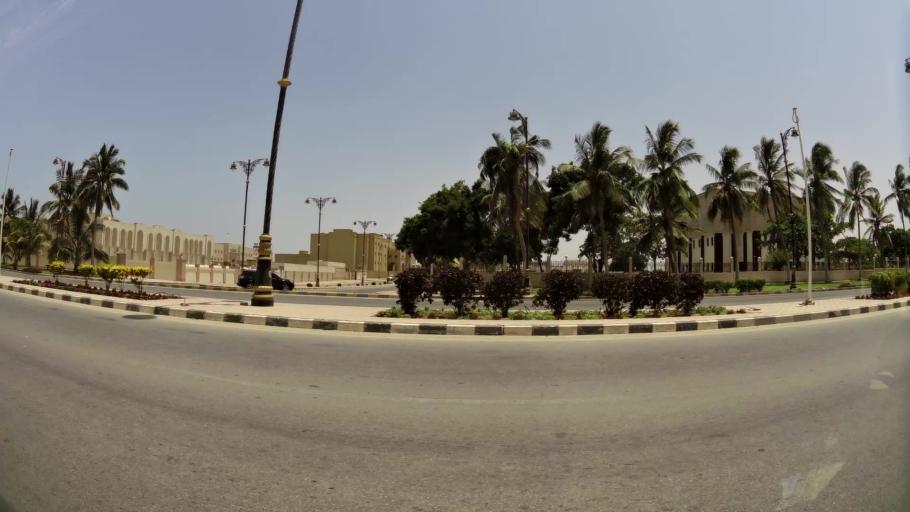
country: OM
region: Zufar
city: Salalah
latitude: 17.0227
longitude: 54.0914
